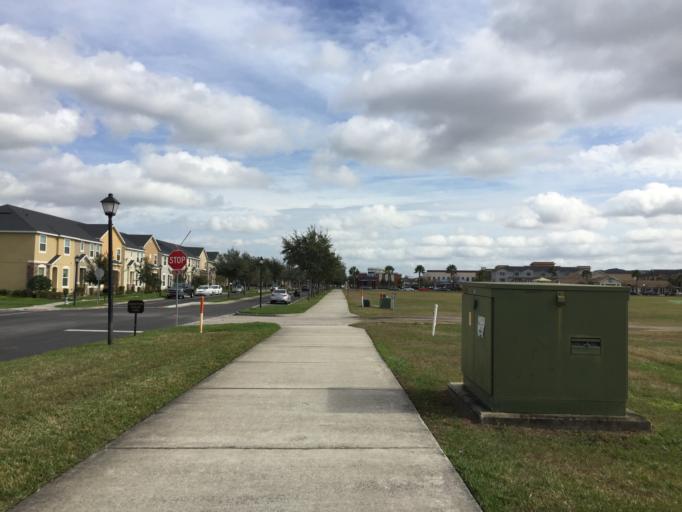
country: US
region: Florida
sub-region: Orange County
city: Bithlo
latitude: 28.5128
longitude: -81.1583
